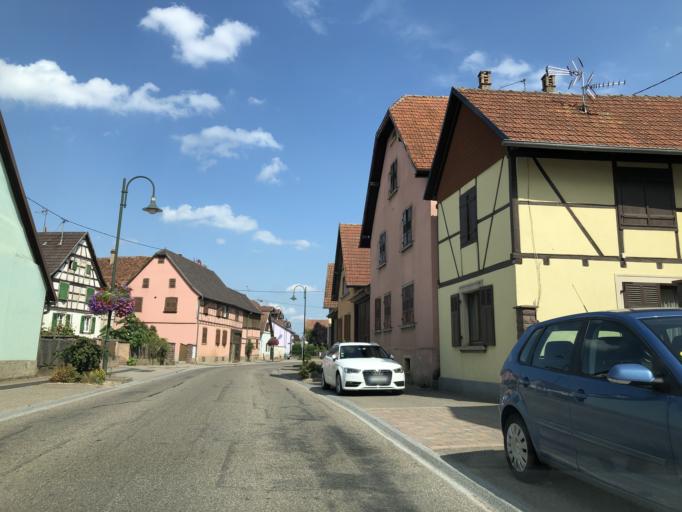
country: FR
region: Alsace
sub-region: Departement du Bas-Rhin
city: Valff
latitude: 48.4221
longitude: 7.5176
